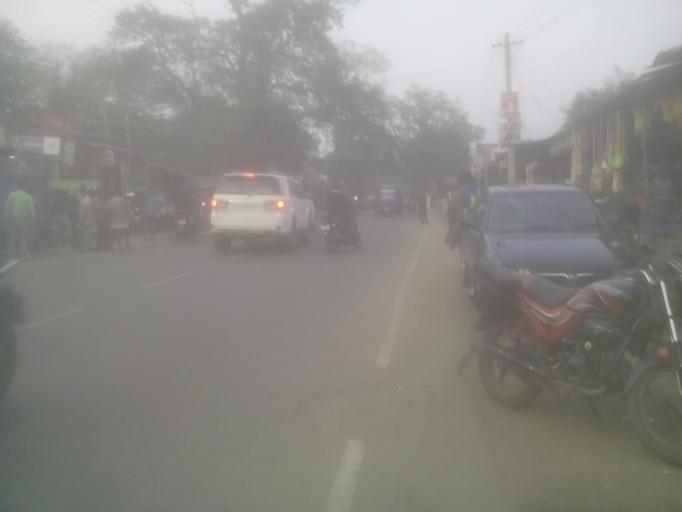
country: IN
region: Jharkhand
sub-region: Dhanbad
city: Dhanbad
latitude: 23.8077
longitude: 86.4321
